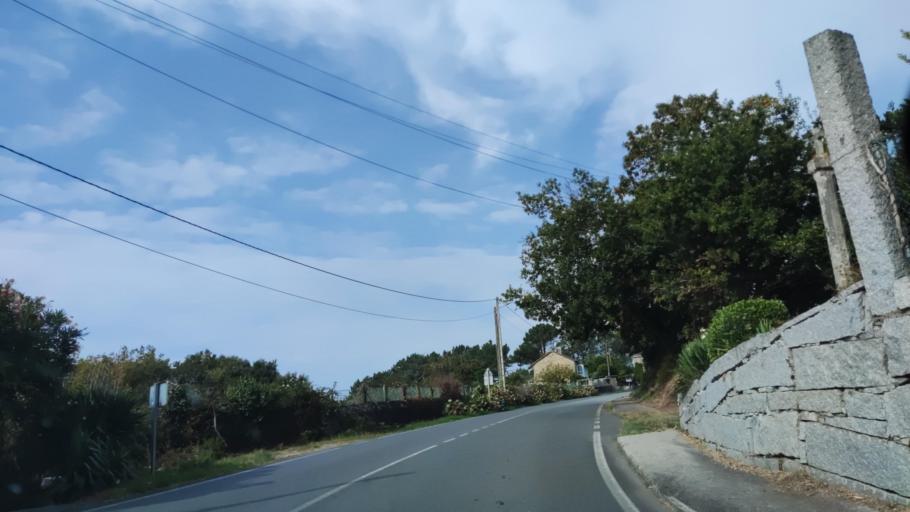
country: ES
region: Galicia
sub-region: Provincia da Coruna
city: Rianxo
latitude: 42.6466
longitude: -8.7853
